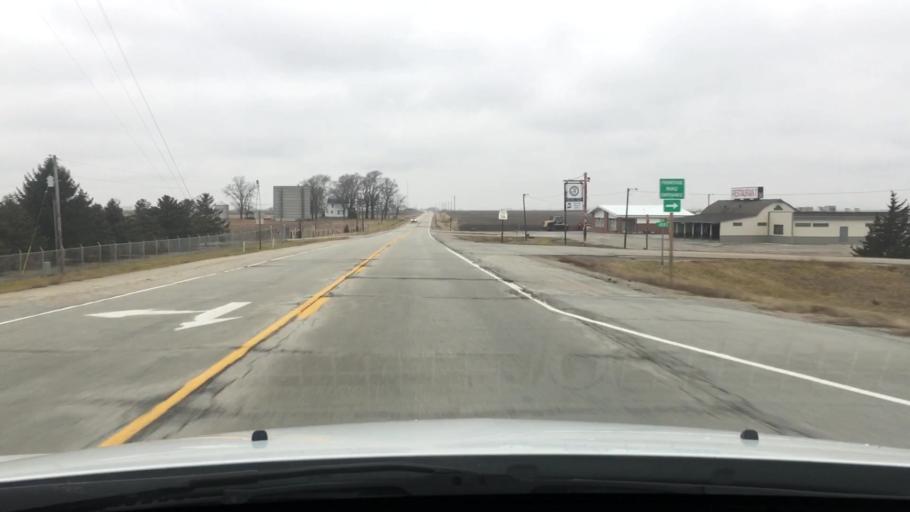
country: US
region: Illinois
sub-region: Iroquois County
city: Clifton
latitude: 40.8840
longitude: -87.9700
